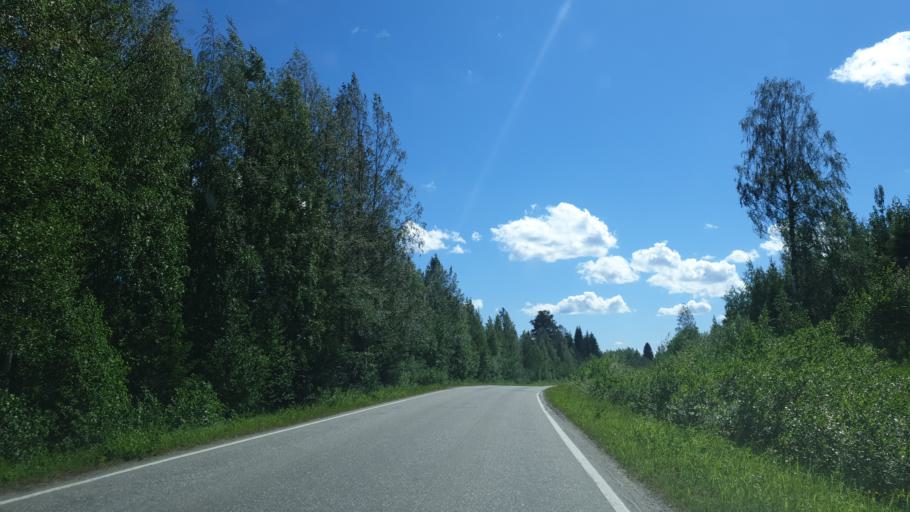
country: FI
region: Northern Savo
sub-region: Koillis-Savo
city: Kaavi
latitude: 62.9898
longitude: 28.5047
